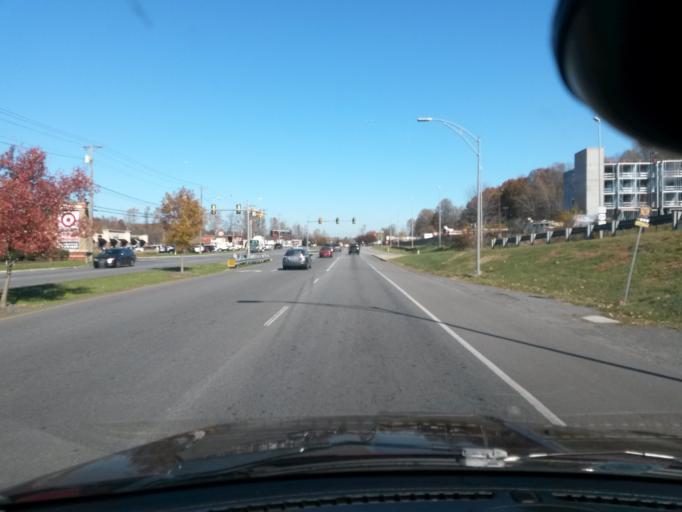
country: US
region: Virginia
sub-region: City of Lynchburg
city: West Lynchburg
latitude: 37.3453
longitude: -79.1879
